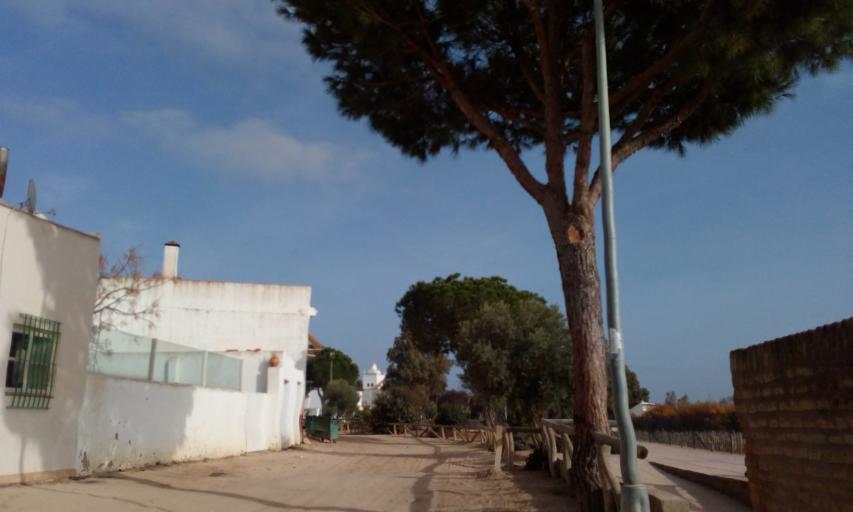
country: ES
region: Andalusia
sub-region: Provincia de Huelva
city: Almonte
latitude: 37.1282
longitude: -6.4828
